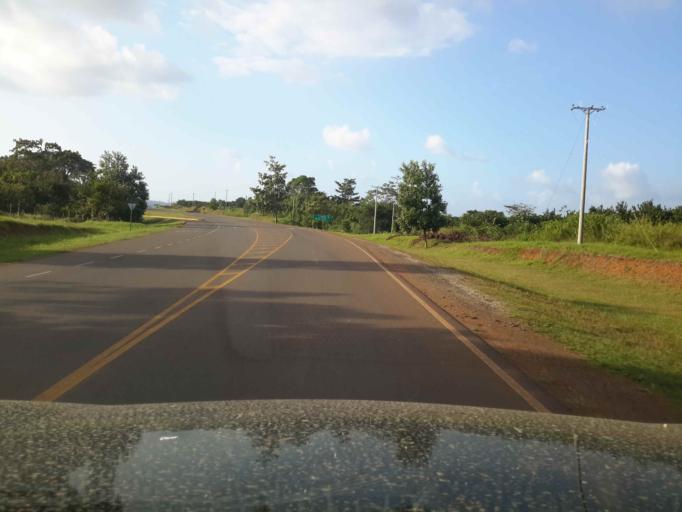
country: NI
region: Rio San Juan
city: San Carlos
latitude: 11.1593
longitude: -84.6584
